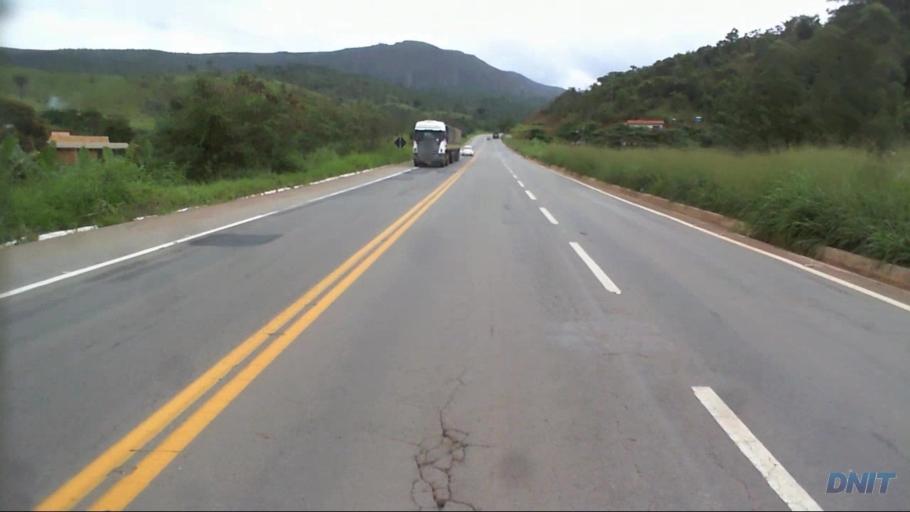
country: BR
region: Minas Gerais
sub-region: Barao De Cocais
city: Barao de Cocais
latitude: -19.8317
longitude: -43.3584
